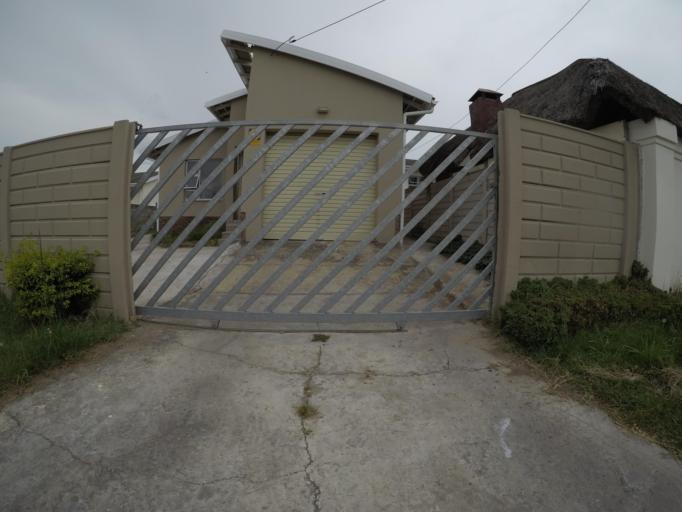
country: ZA
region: Eastern Cape
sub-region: Buffalo City Metropolitan Municipality
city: East London
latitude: -32.9998
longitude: 27.8472
